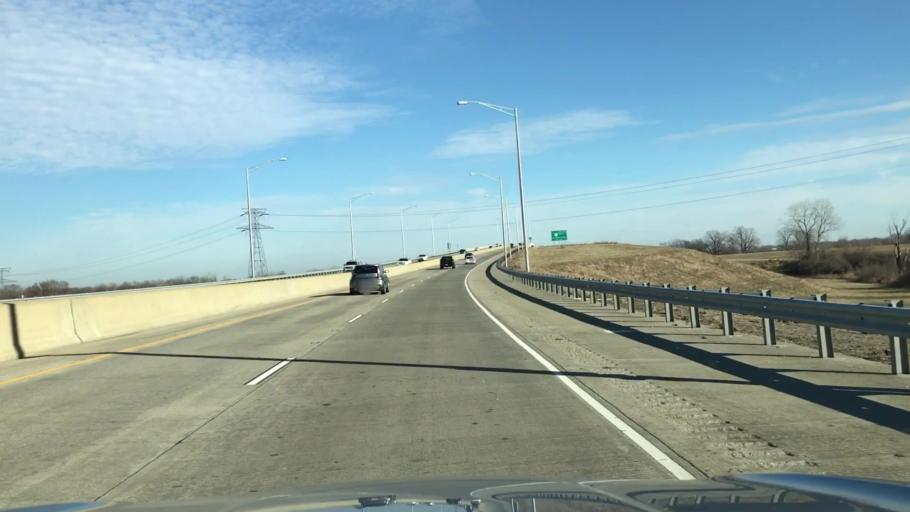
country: US
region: Missouri
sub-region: Saint Louis County
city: Glasgow Village
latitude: 38.7654
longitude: -90.1427
